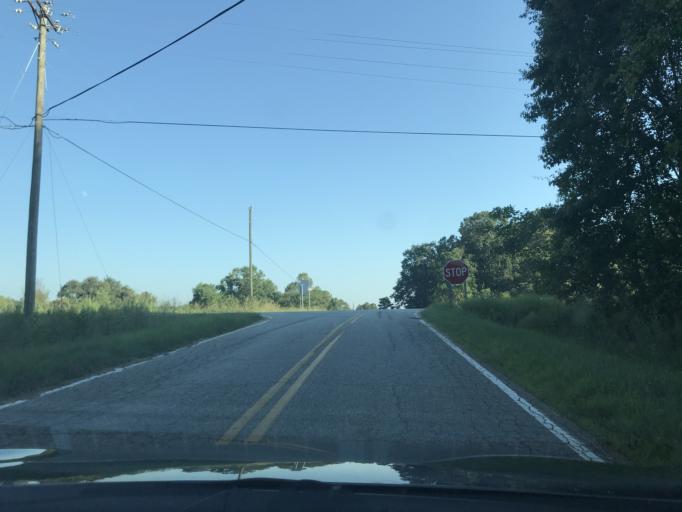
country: US
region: South Carolina
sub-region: Spartanburg County
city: Mayo
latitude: 35.1167
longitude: -81.7847
